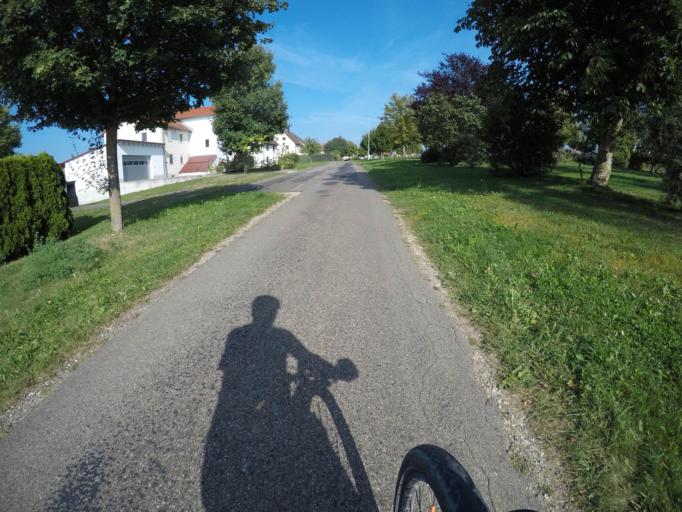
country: DE
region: Baden-Wuerttemberg
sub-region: Regierungsbezirk Stuttgart
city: Bohmenkirch
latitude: 48.6378
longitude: 9.9677
